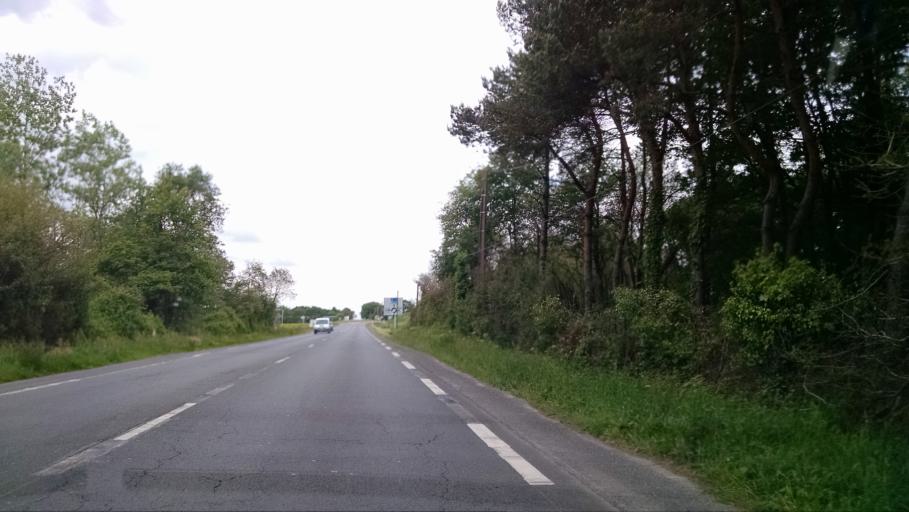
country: FR
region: Pays de la Loire
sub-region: Departement de la Loire-Atlantique
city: Le Bignon
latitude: 47.1155
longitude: -1.4821
